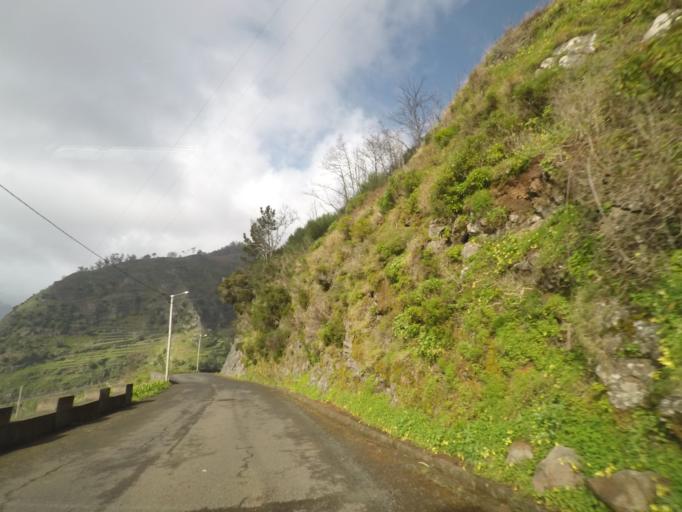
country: PT
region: Madeira
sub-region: Ribeira Brava
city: Campanario
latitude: 32.6990
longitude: -17.0264
